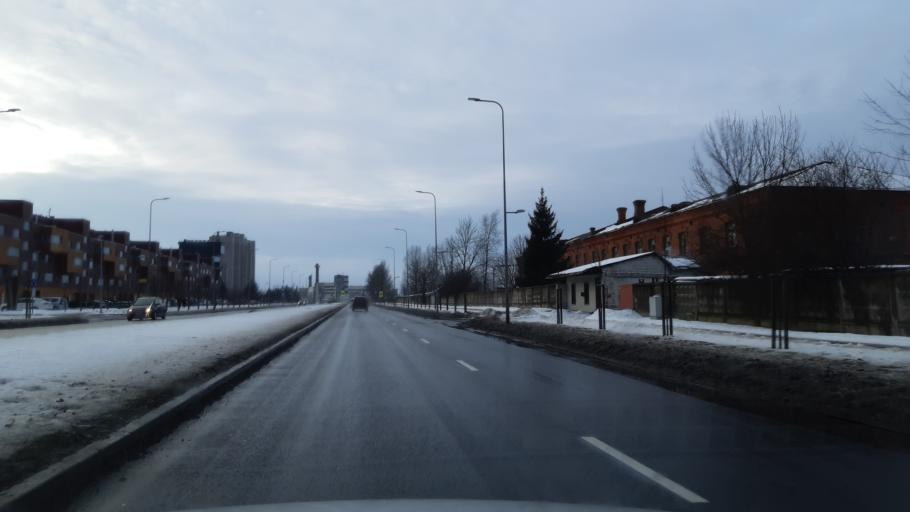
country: LT
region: Kauno apskritis
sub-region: Kaunas
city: Aleksotas
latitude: 54.8751
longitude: 23.9112
